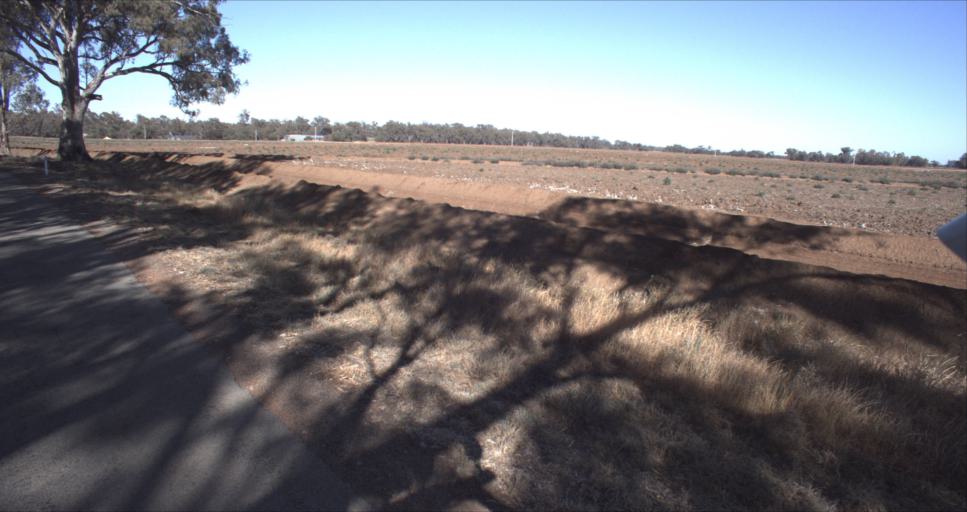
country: AU
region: New South Wales
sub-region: Leeton
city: Leeton
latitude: -34.6095
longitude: 146.2607
